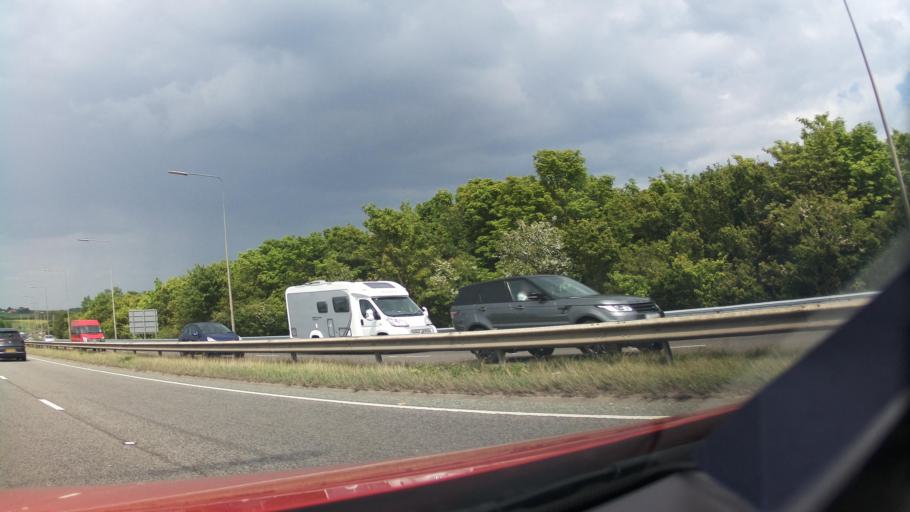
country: GB
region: England
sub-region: County Durham
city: Shotton
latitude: 54.7874
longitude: -1.3670
